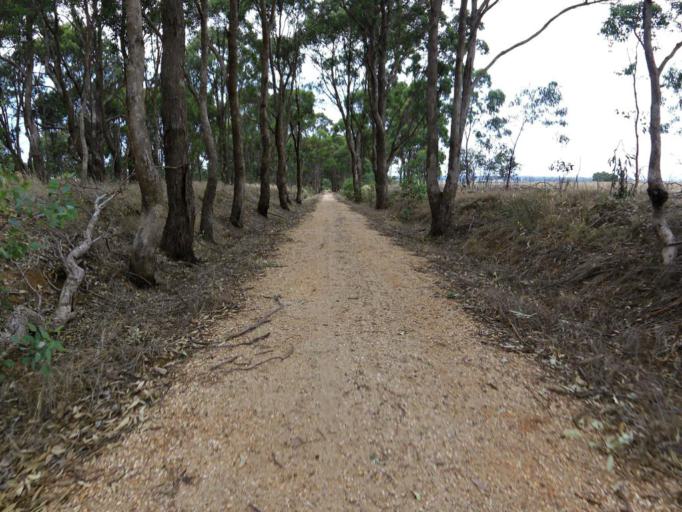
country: AU
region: Victoria
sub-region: Greater Bendigo
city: Kennington
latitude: -36.8555
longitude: 144.6185
